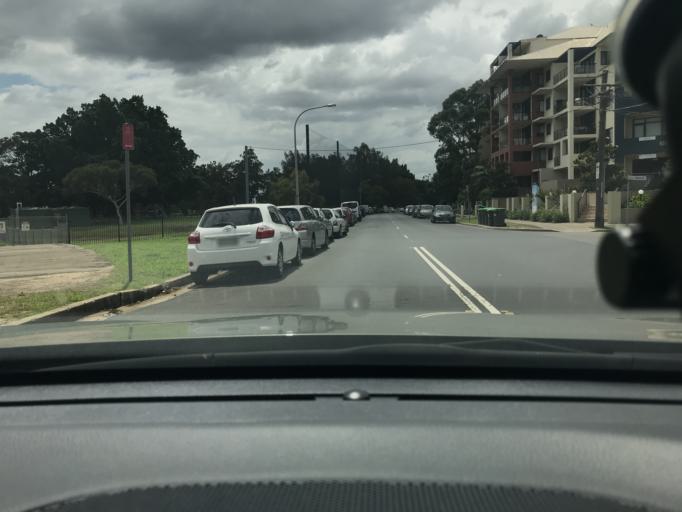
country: AU
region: New South Wales
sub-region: Ashfield
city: Croydon
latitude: -33.8686
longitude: 151.1189
